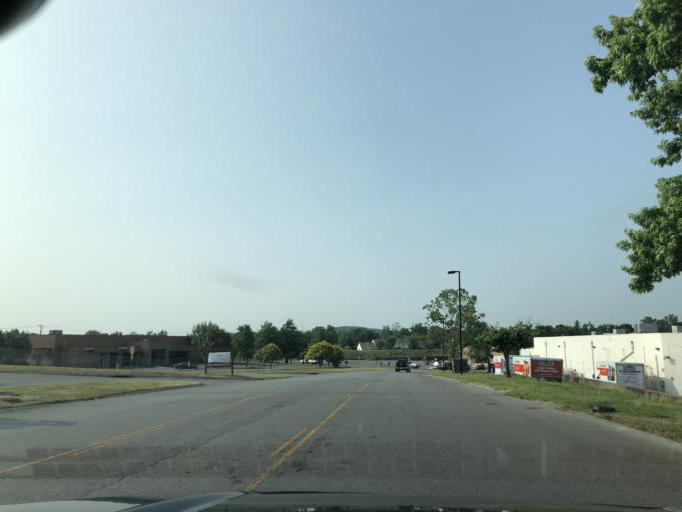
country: US
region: Tennessee
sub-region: Rutherford County
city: La Vergne
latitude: 36.0494
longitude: -86.6461
